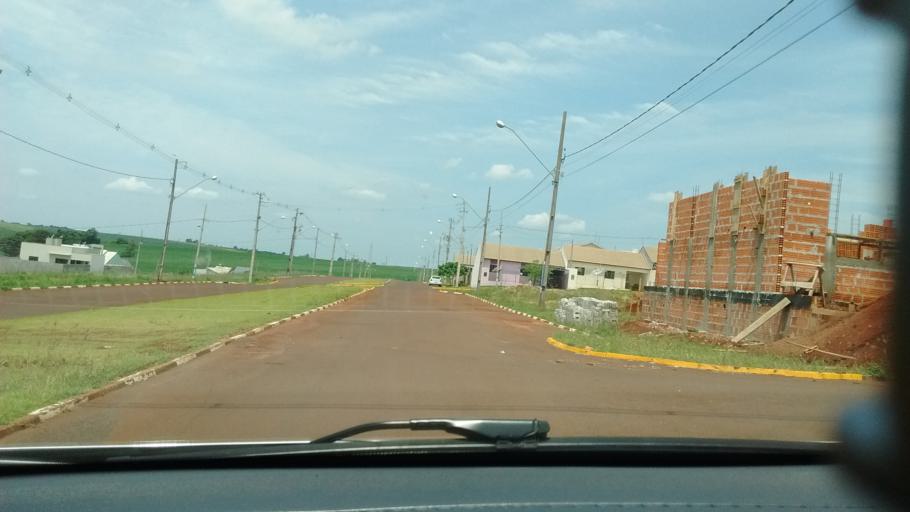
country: BR
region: Parana
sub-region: Corbelia
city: Corbelia
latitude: -24.5502
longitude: -52.9783
